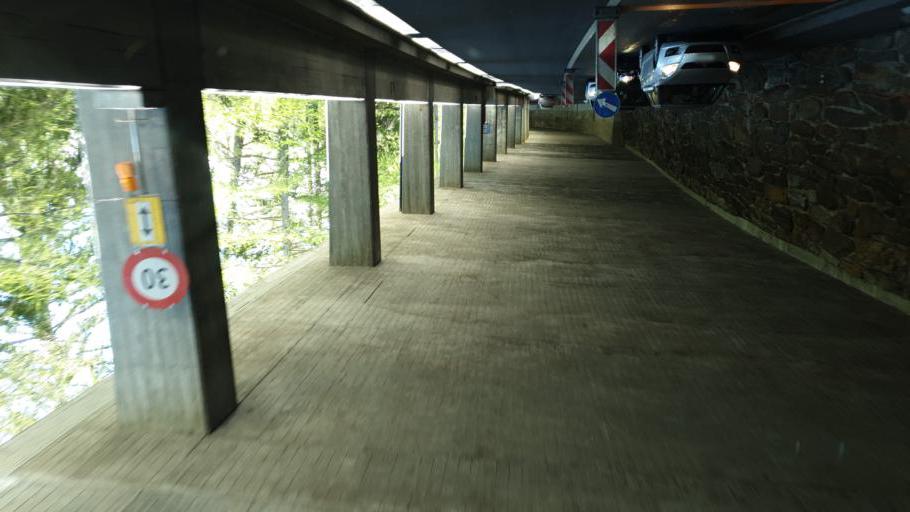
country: CH
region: Valais
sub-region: Brig District
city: Brig
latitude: 46.2743
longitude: 8.0395
